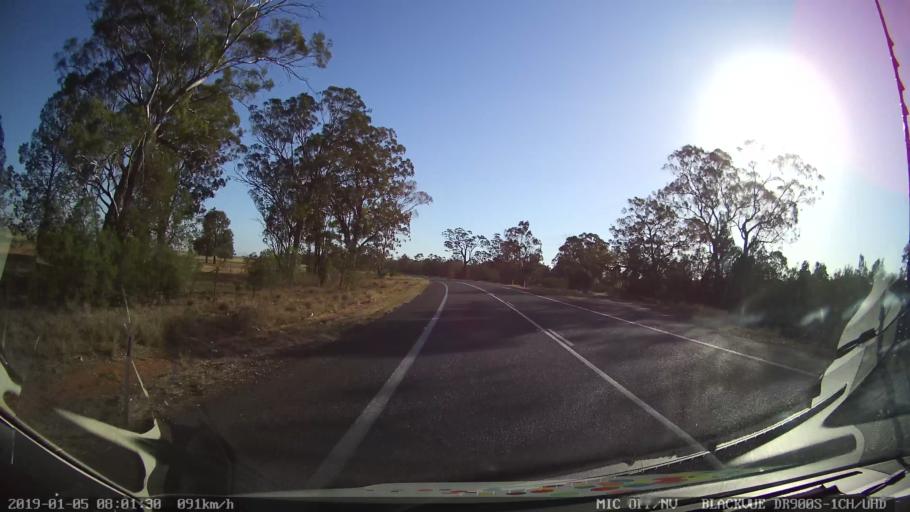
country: AU
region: New South Wales
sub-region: Gilgandra
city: Gilgandra
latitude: -31.6863
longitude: 148.7033
